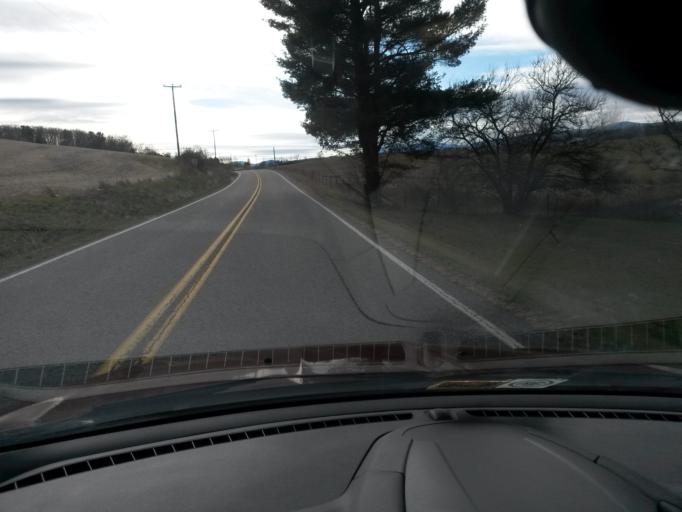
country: US
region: Virginia
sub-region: City of Staunton
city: Staunton
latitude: 38.2625
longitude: -79.1548
